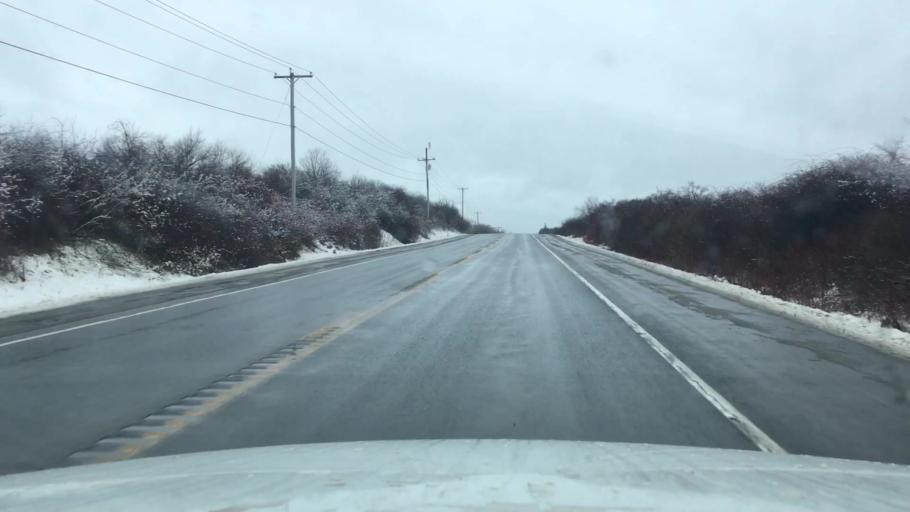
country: US
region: Maine
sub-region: Knox County
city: Thomaston
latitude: 44.0876
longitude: -69.1572
